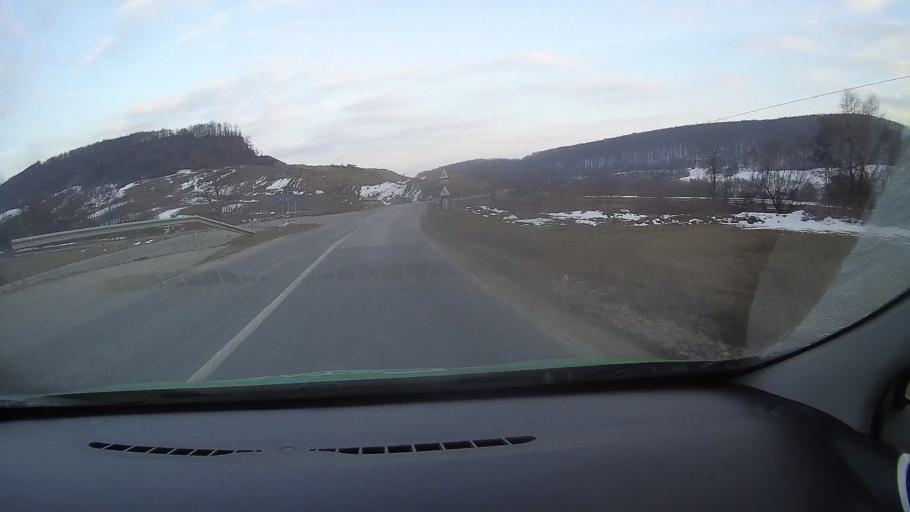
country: RO
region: Harghita
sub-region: Comuna Lupeni
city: Lupeni
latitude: 46.3604
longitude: 25.1873
